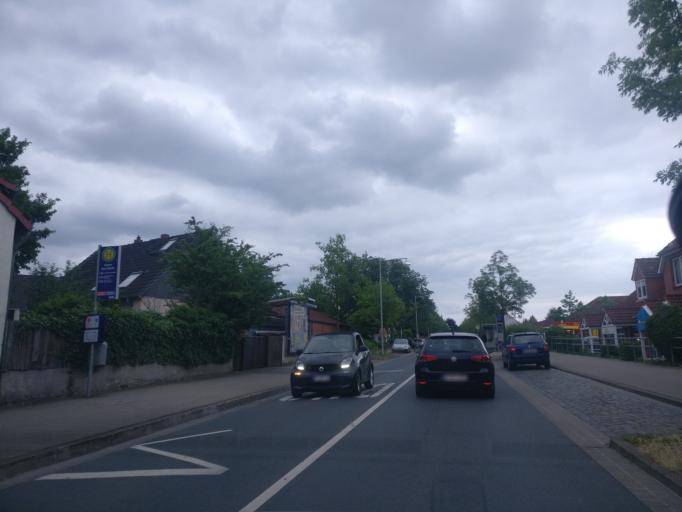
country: DE
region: Lower Saxony
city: Laatzen
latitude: 52.3421
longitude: 9.8270
